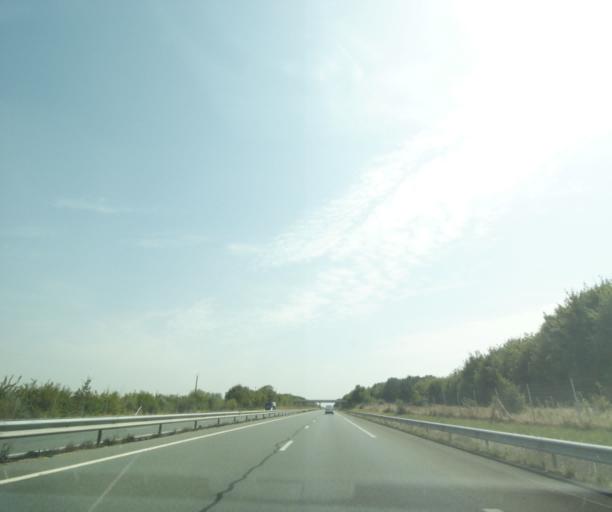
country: FR
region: Pays de la Loire
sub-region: Departement de la Vendee
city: Nalliers
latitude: 46.5074
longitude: -1.0073
